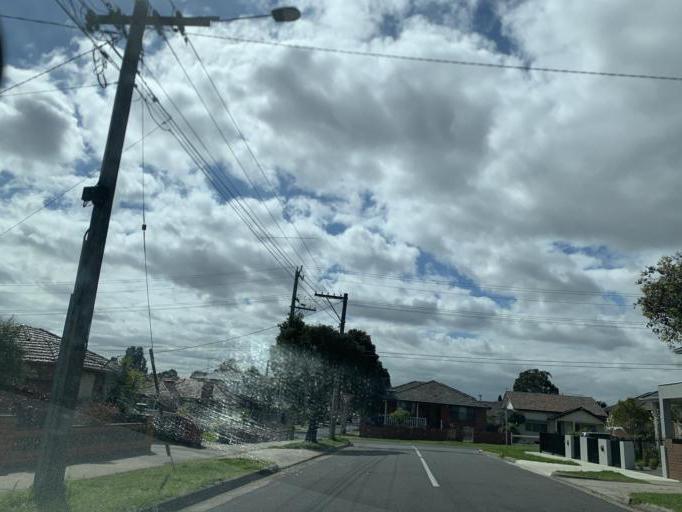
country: AU
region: Victoria
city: Thornbury
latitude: -37.7416
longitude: 144.9883
